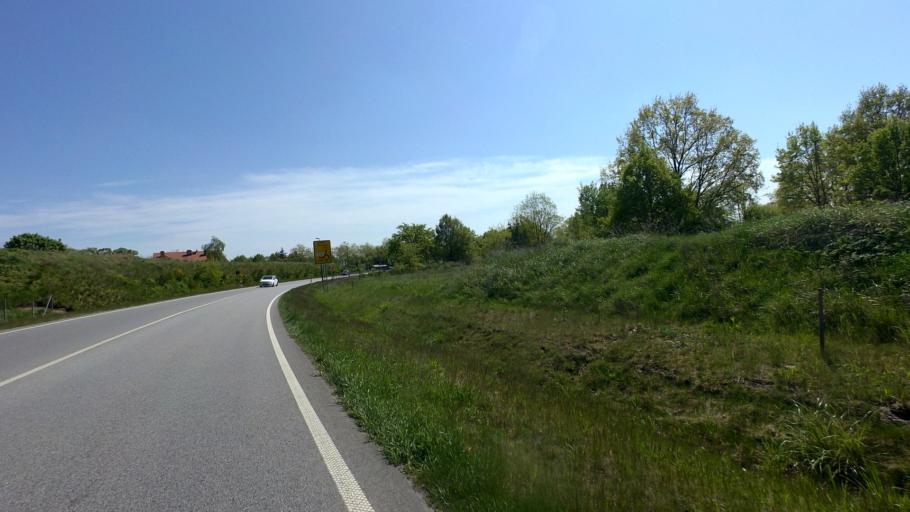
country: DE
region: Brandenburg
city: Konigs Wusterhausen
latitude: 52.2766
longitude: 13.6293
